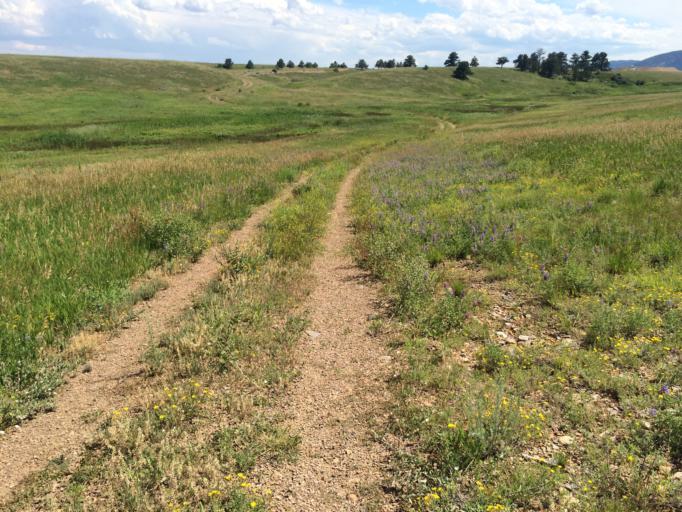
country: US
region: Colorado
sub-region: Boulder County
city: Superior
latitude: 39.8987
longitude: -105.2219
